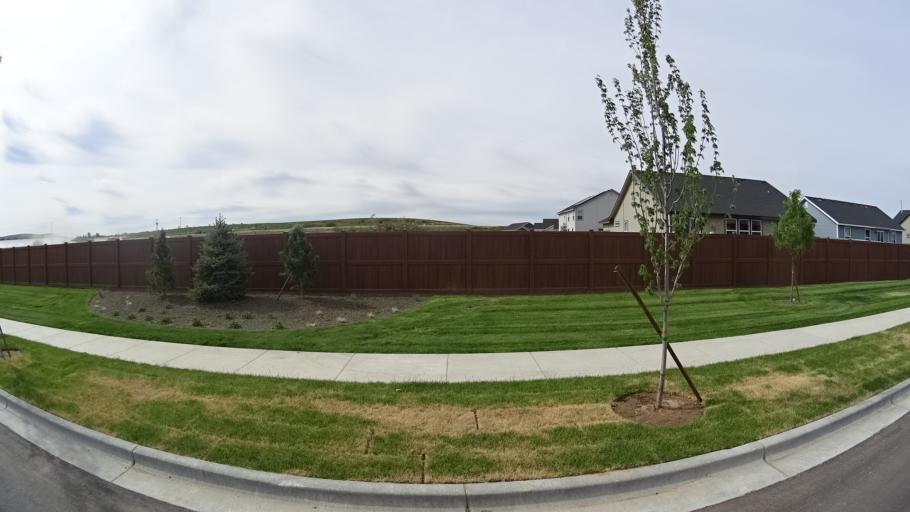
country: US
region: Idaho
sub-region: Ada County
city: Garden City
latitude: 43.5329
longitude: -116.2967
